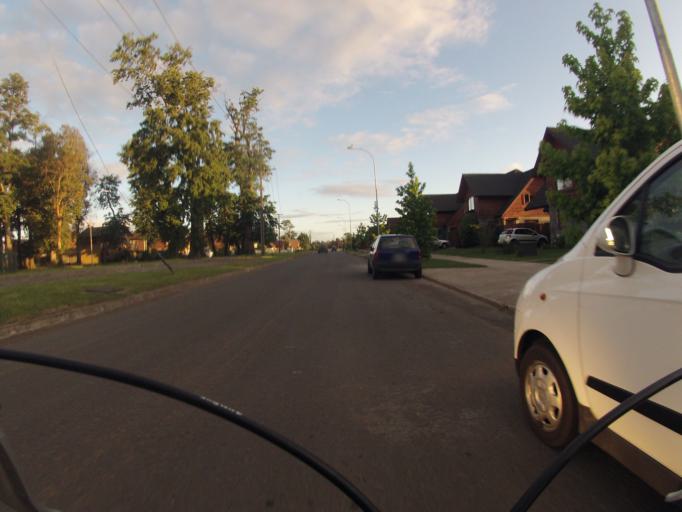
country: CL
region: Araucania
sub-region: Provincia de Cautin
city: Temuco
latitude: -38.7413
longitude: -72.6502
